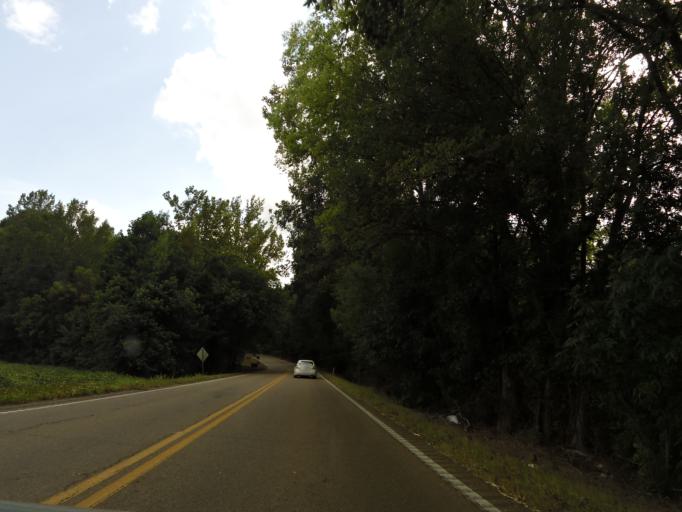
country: US
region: Mississippi
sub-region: Alcorn County
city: Farmington
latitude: 35.0055
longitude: -88.4612
